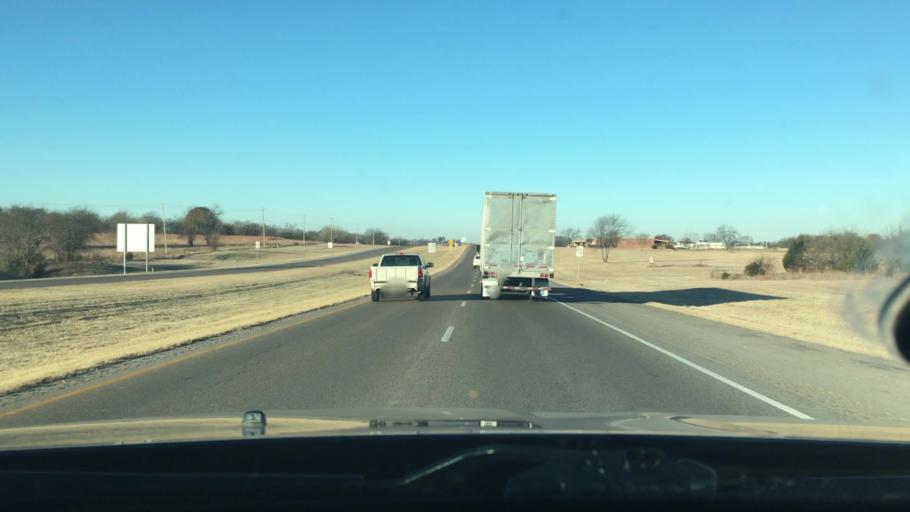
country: US
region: Oklahoma
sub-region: Murray County
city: Sulphur
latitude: 34.5064
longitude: -97.0143
